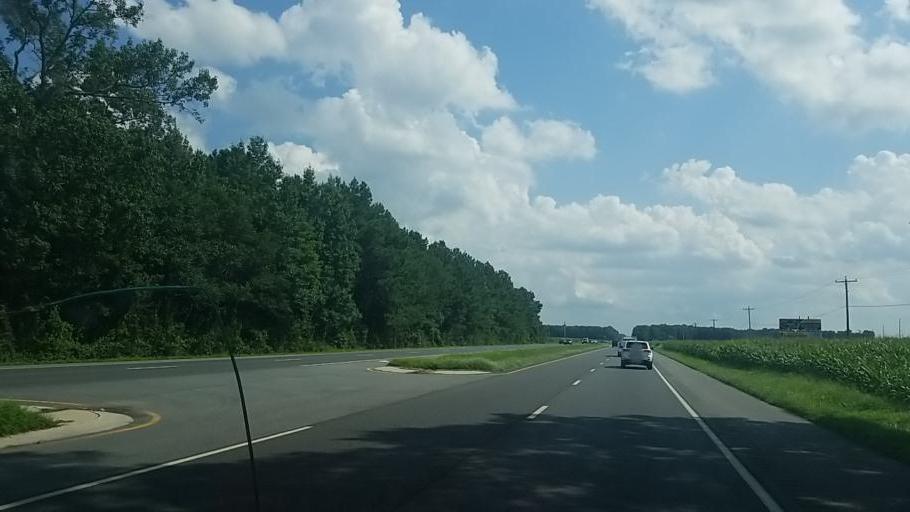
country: US
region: Delaware
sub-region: Sussex County
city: Selbyville
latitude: 38.4977
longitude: -75.2371
